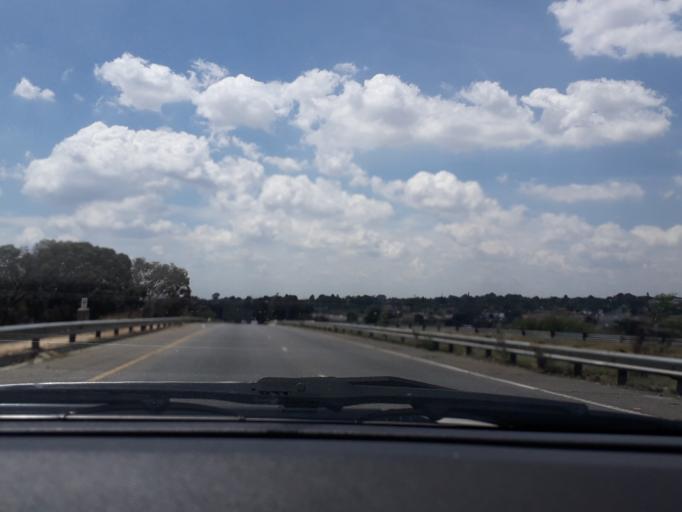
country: ZA
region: Gauteng
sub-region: City of Johannesburg Metropolitan Municipality
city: Johannesburg
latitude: -26.2586
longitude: 27.9831
